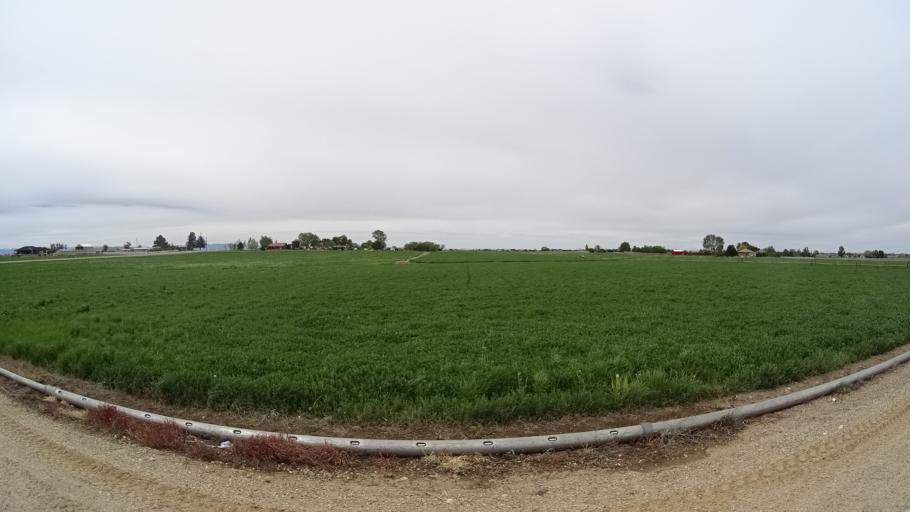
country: US
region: Idaho
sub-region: Ada County
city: Kuna
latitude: 43.4975
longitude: -116.3737
